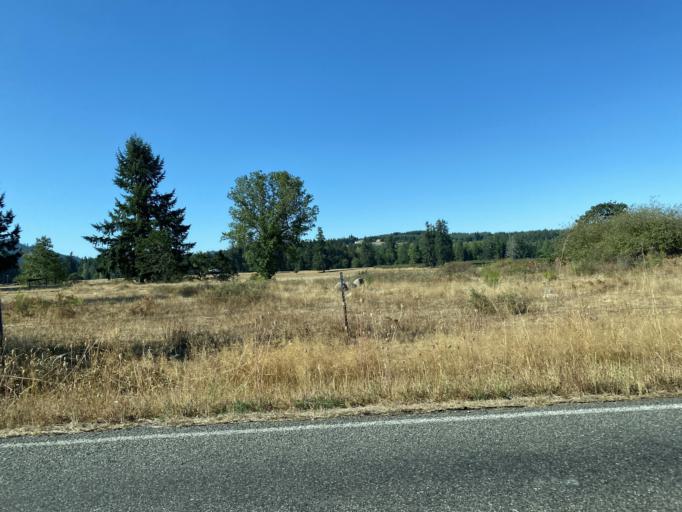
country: US
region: Washington
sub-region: Thurston County
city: Rainier
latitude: 46.8881
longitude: -122.7479
